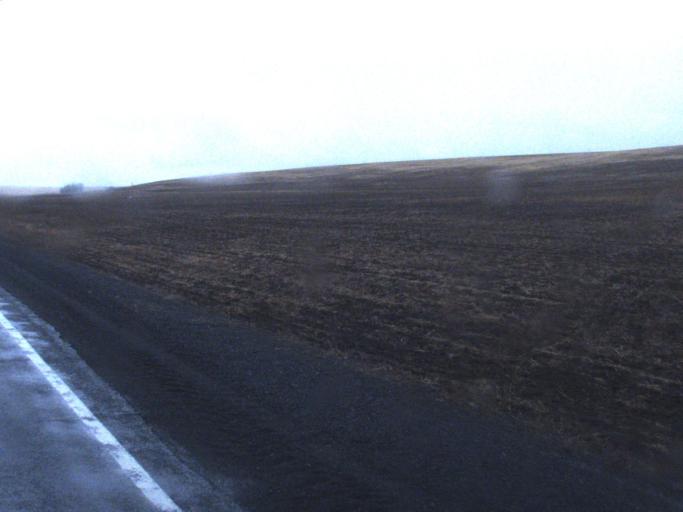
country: US
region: Washington
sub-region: Lincoln County
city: Davenport
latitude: 47.3943
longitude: -118.1506
